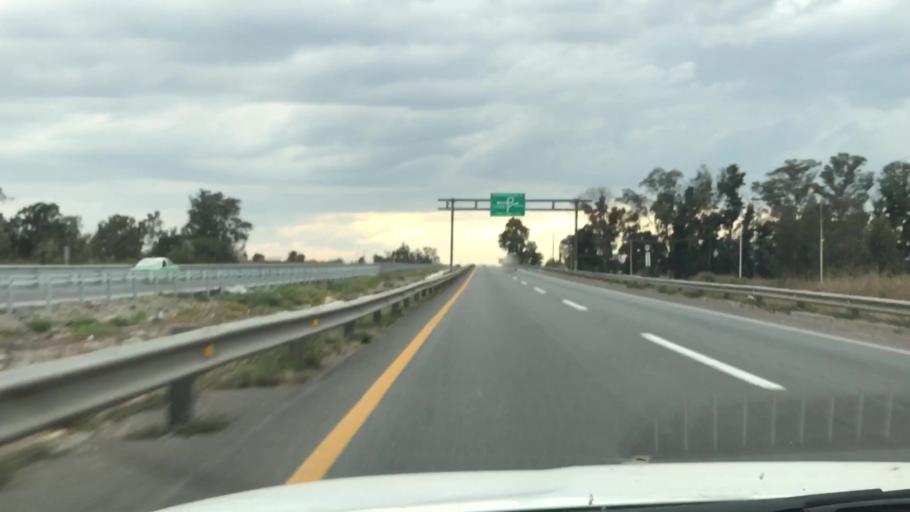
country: MX
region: Guanajuato
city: Irapuato
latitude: 20.6493
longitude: -101.3563
